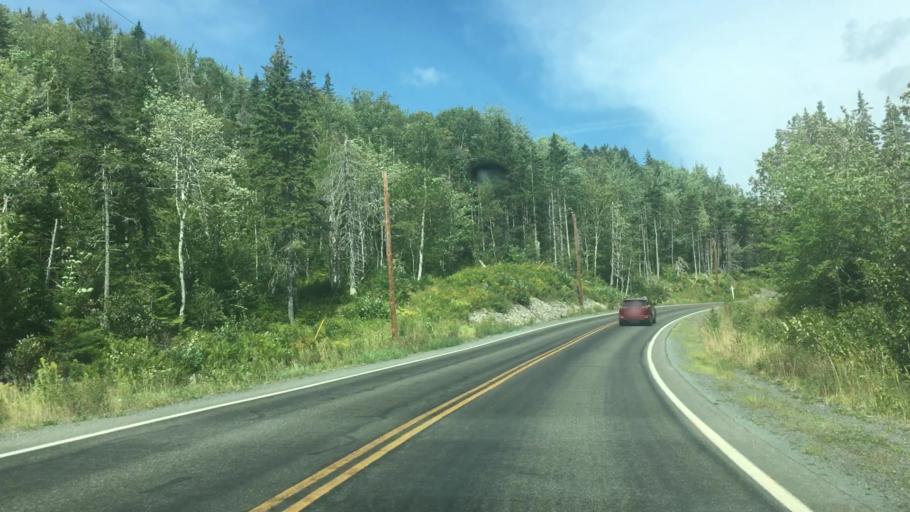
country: CA
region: Nova Scotia
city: Sydney Mines
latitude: 46.2071
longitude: -60.6227
